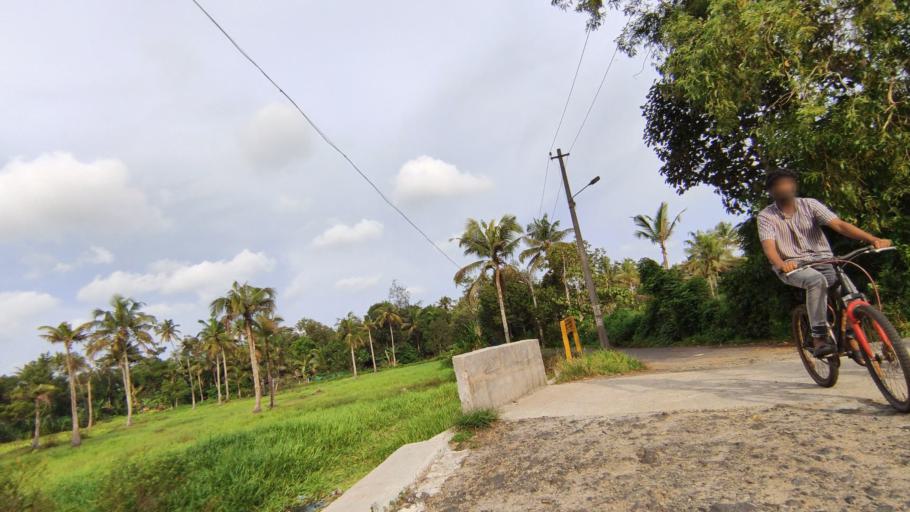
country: IN
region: Kerala
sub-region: Alappuzha
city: Shertallai
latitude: 9.6236
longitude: 76.3369
